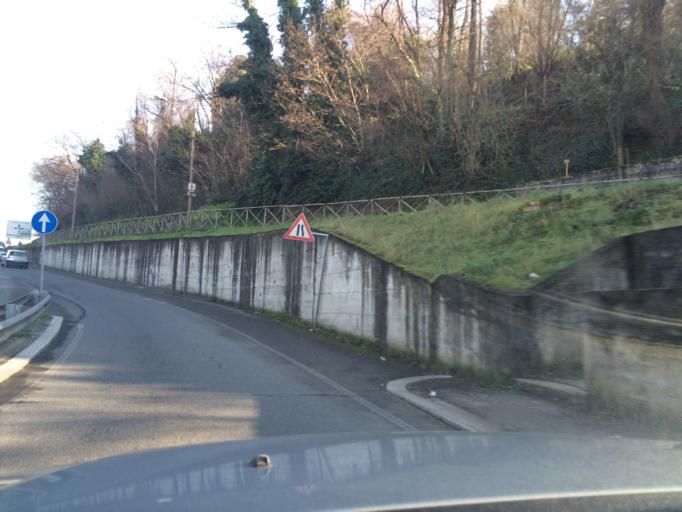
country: IT
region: Umbria
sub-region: Provincia di Terni
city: Terni
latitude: 42.5578
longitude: 12.6547
